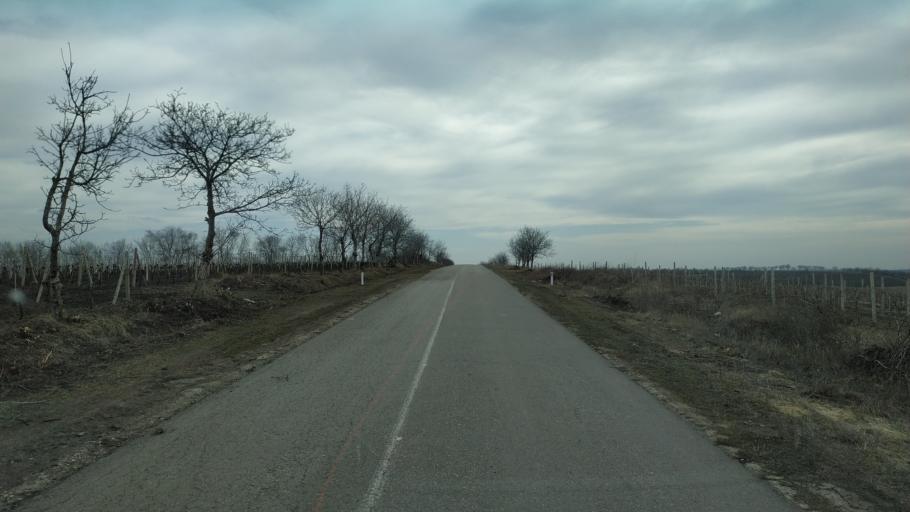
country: MD
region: Nisporeni
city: Nisporeni
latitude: 46.9525
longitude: 28.2379
